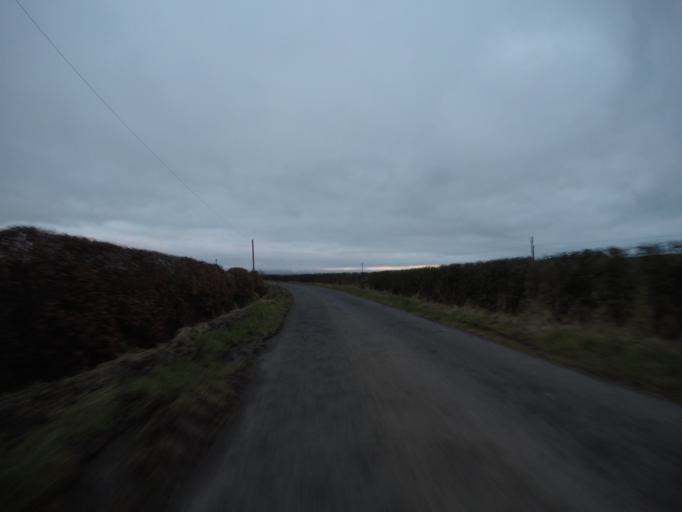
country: GB
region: Scotland
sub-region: North Ayrshire
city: Dalry
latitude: 55.6821
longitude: -4.7283
